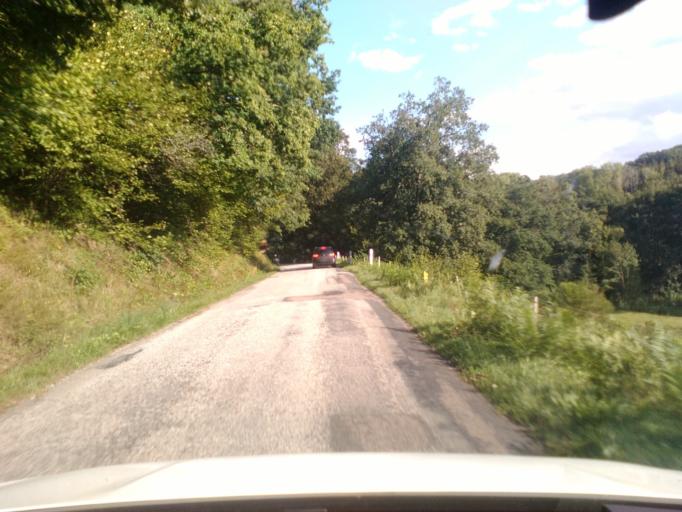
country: FR
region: Lorraine
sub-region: Departement des Vosges
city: Corcieux
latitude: 48.1580
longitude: 6.9085
